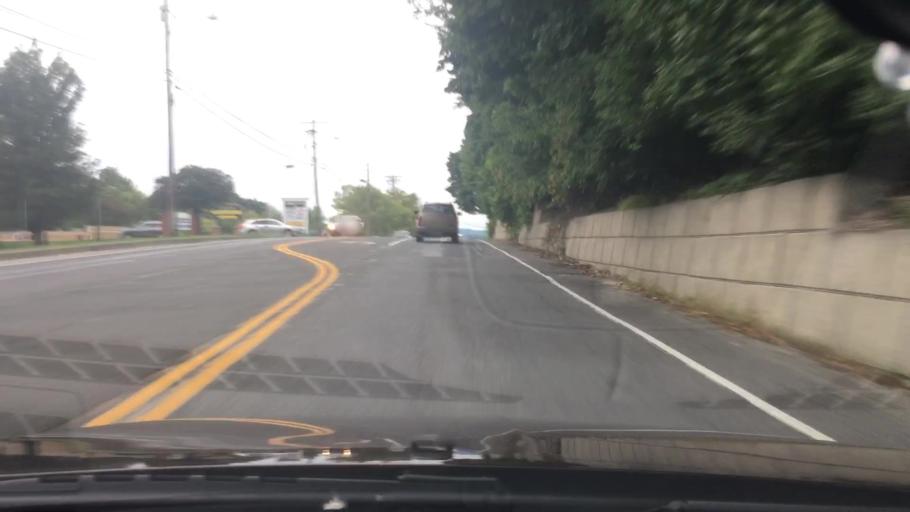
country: US
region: New York
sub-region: Dutchess County
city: Arlington
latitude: 41.6989
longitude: -73.8808
